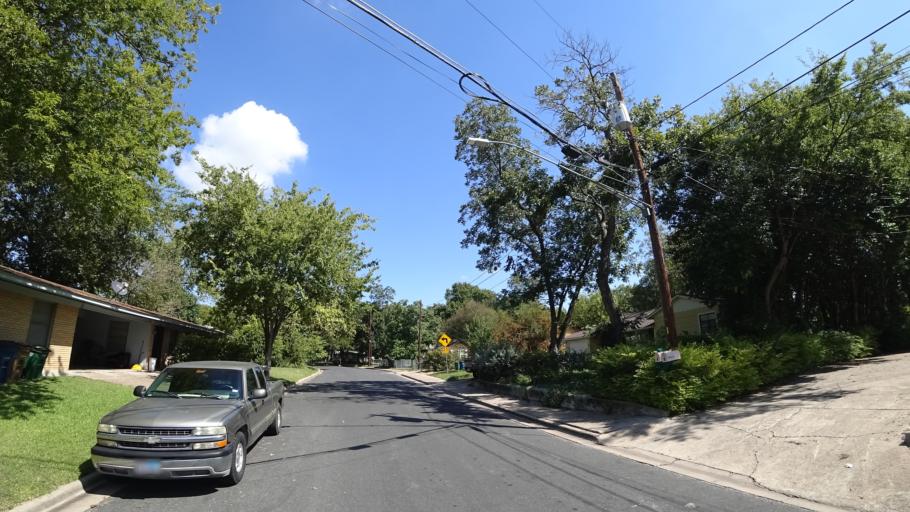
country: US
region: Texas
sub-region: Travis County
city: Austin
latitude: 30.3303
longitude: -97.7170
